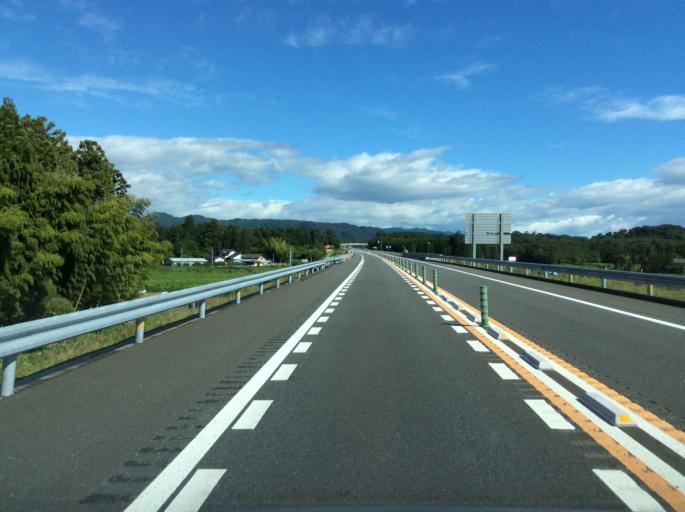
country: JP
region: Fukushima
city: Namie
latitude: 37.4850
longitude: 140.9531
